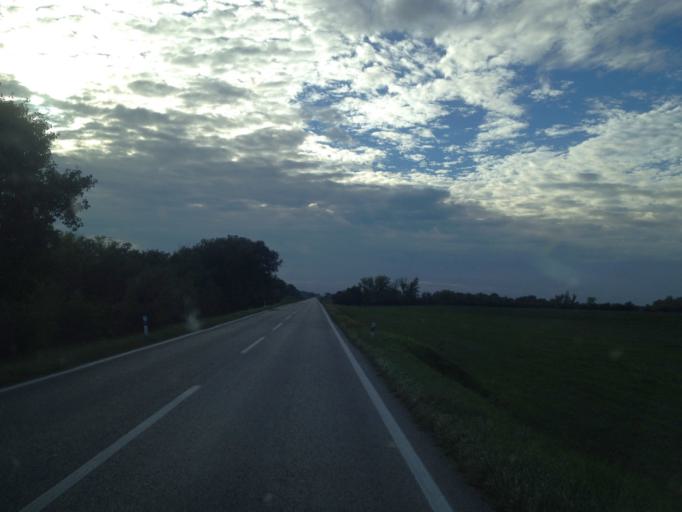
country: HU
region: Komarom-Esztergom
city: Almasfuzito
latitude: 47.7427
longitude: 18.2665
